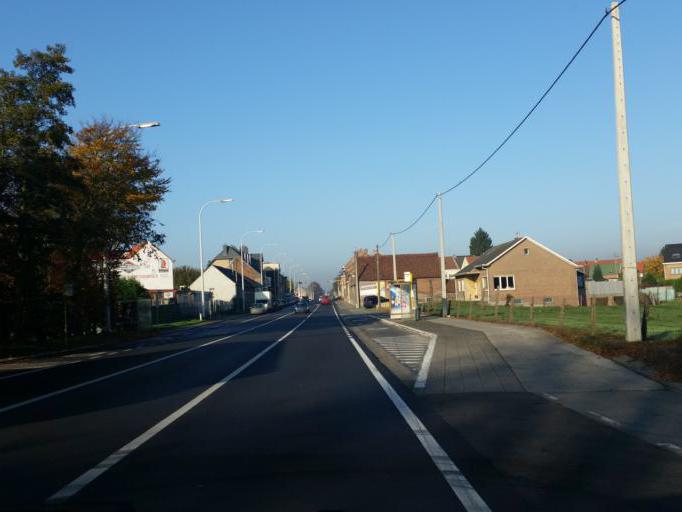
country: BE
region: Flanders
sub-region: Provincie Vlaams-Brabant
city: Asse
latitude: 50.8975
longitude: 4.2326
